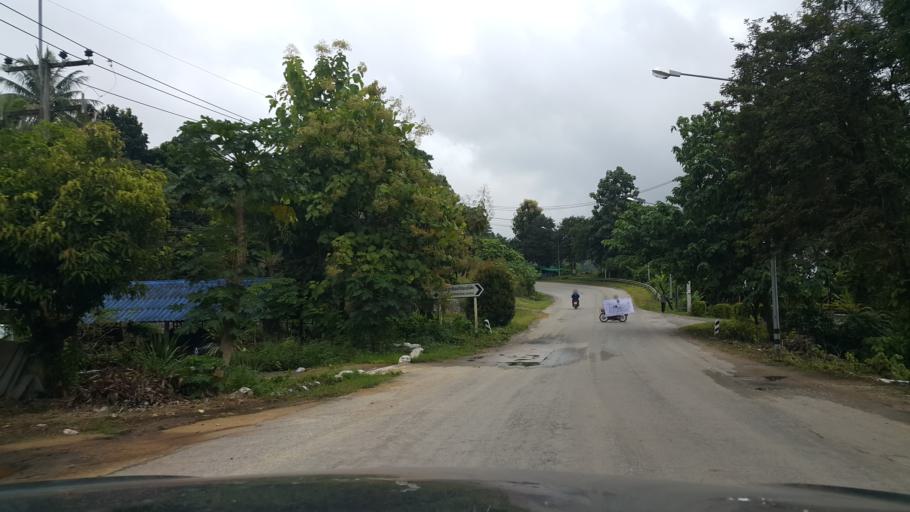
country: TH
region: Chiang Mai
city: Samoeng
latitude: 18.7884
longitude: 98.8390
